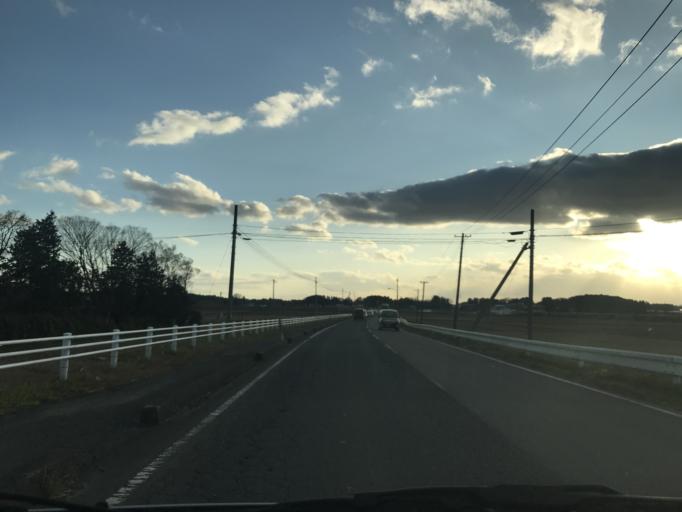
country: JP
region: Miyagi
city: Kogota
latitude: 38.6437
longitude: 141.0738
